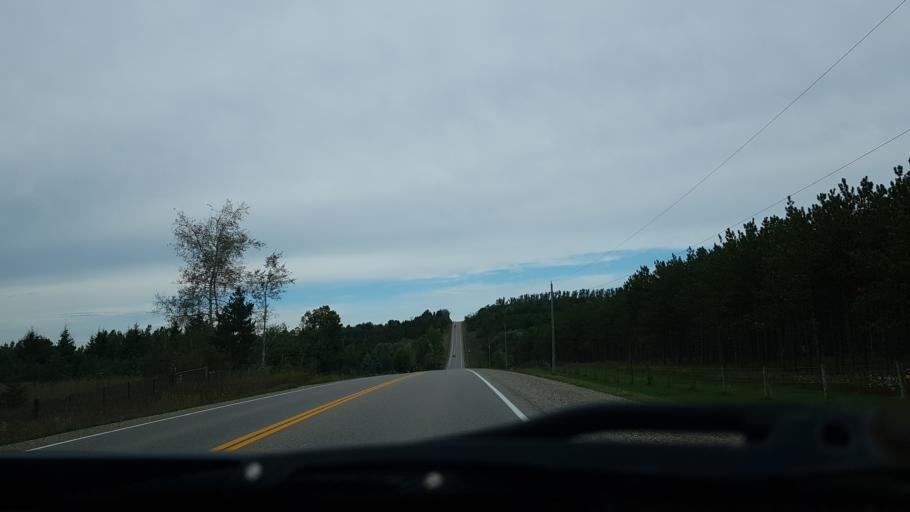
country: CA
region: Ontario
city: Shelburne
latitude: 44.0870
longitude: -80.0202
